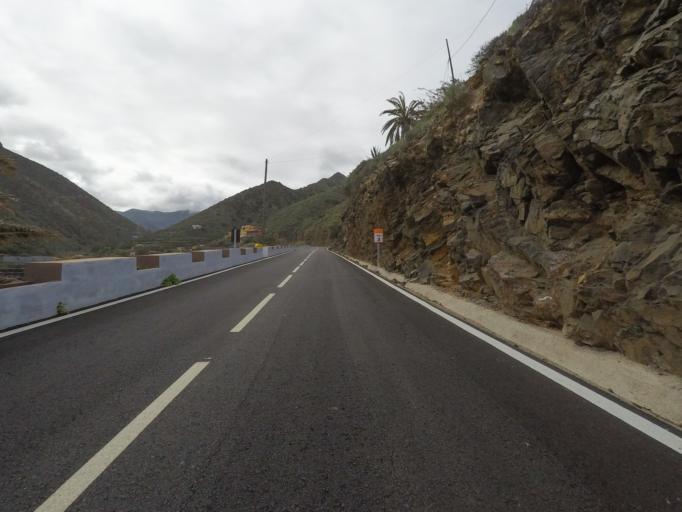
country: ES
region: Canary Islands
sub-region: Provincia de Santa Cruz de Tenerife
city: Vallehermosa
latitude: 28.2017
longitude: -17.2547
